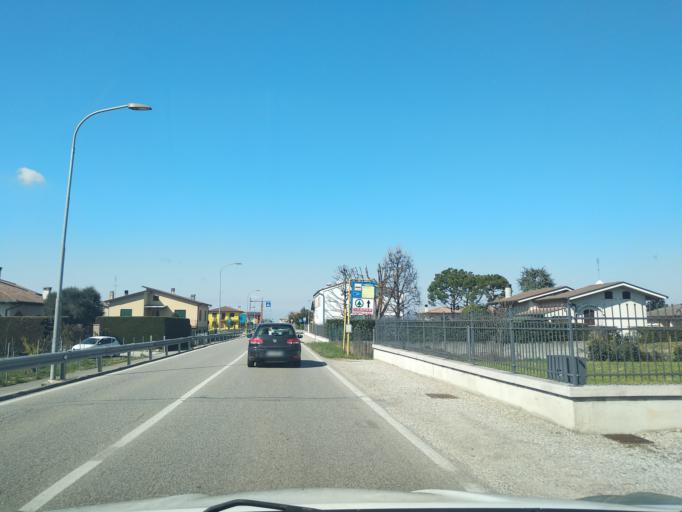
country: IT
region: Veneto
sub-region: Provincia di Padova
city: Taggi
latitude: 45.4606
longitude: 11.8215
